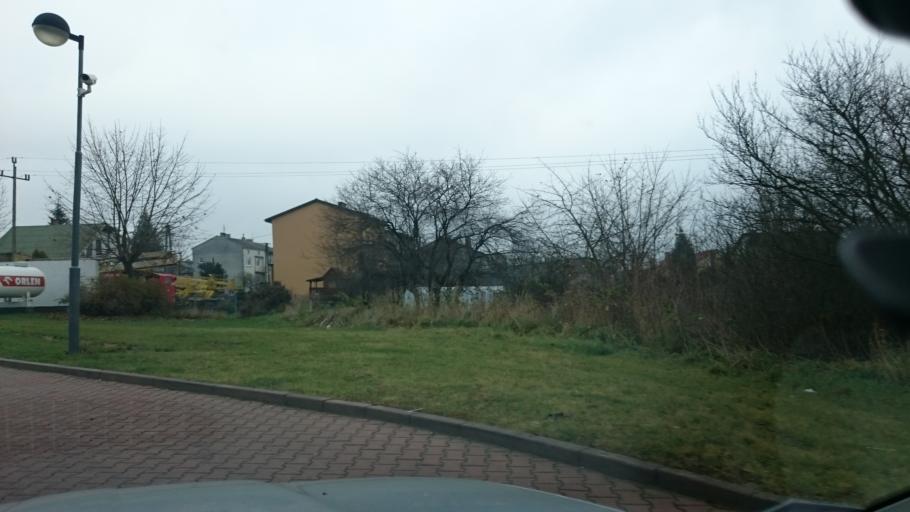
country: PL
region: Swietokrzyskie
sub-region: Powiat konecki
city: Konskie
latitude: 51.1865
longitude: 20.3969
